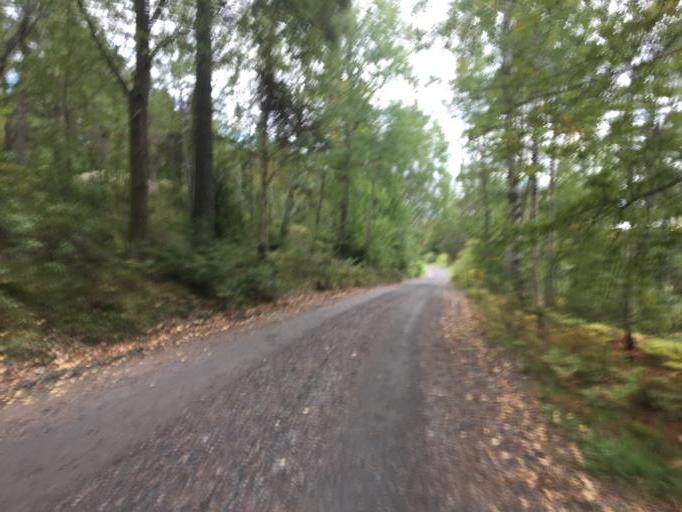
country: SE
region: Soedermanland
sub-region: Eskilstuna Kommun
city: Arla
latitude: 59.4546
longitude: 16.6813
